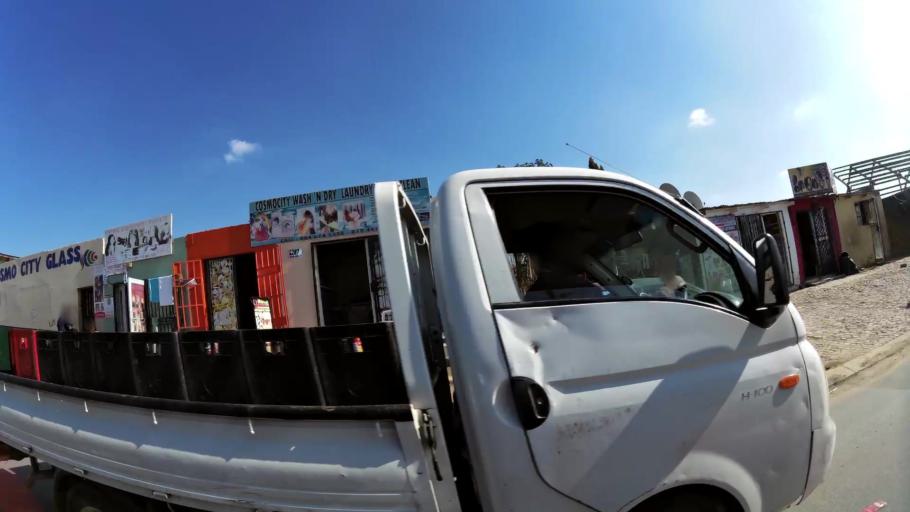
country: ZA
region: Gauteng
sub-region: West Rand District Municipality
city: Muldersdriseloop
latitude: -26.0233
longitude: 27.9288
